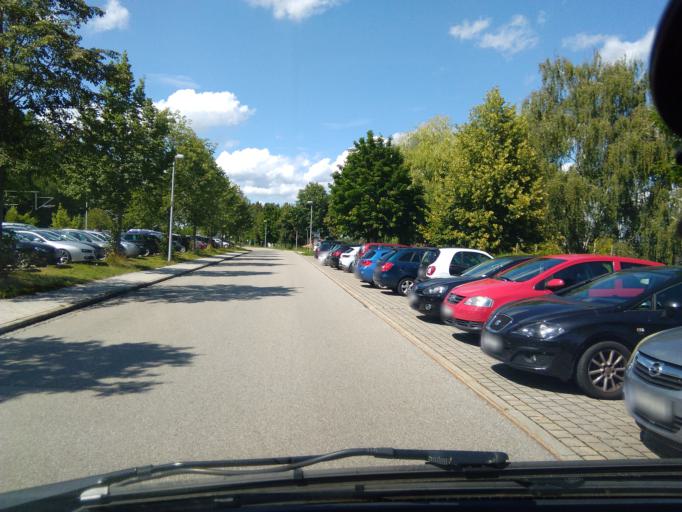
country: DE
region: Bavaria
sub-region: Upper Bavaria
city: Assling
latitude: 47.9905
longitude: 11.9937
